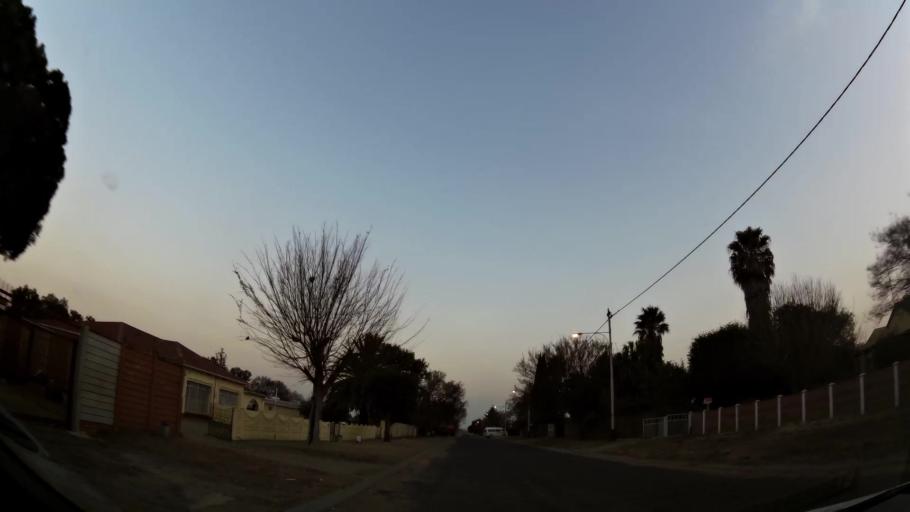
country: ZA
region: Gauteng
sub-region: Ekurhuleni Metropolitan Municipality
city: Nigel
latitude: -26.3539
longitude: 28.4400
